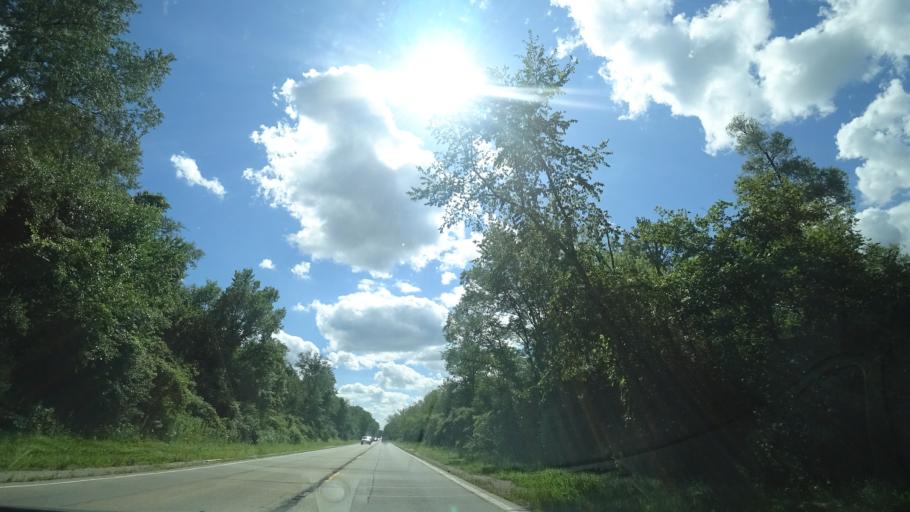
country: US
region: Illinois
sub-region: Will County
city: Mokena
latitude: 41.5546
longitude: -87.9209
